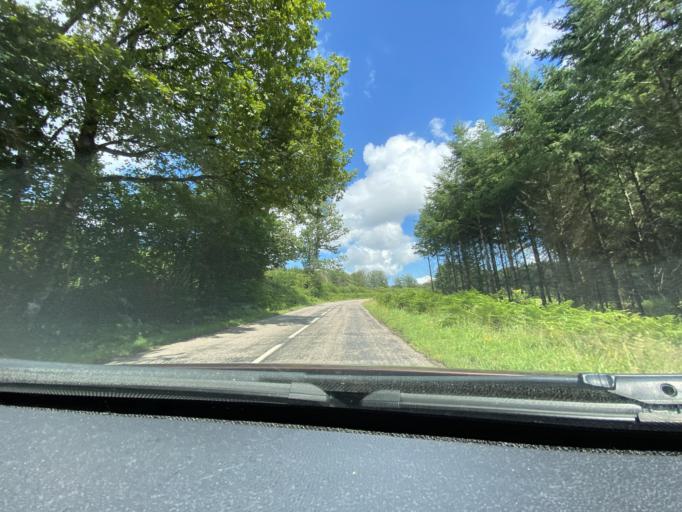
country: FR
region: Bourgogne
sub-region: Departement de la Cote-d'Or
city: Saulieu
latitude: 47.2578
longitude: 4.0967
